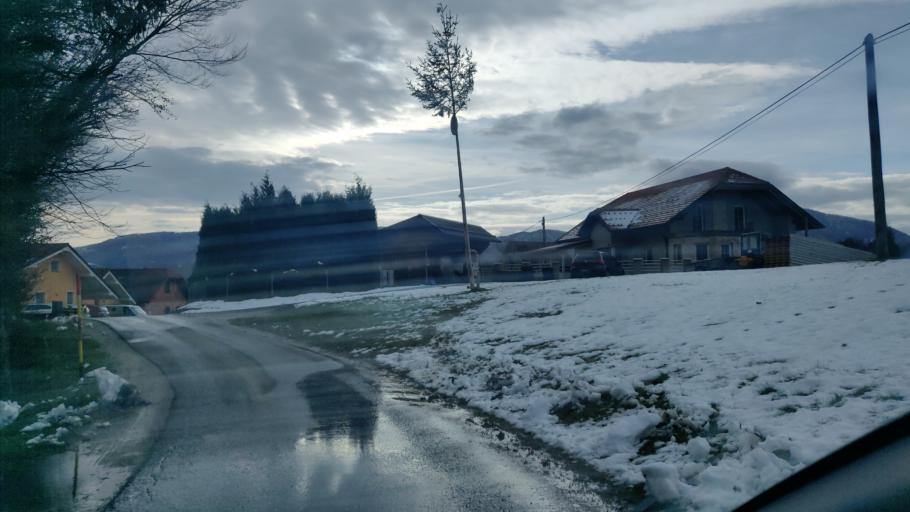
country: SI
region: Makole
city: Makole
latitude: 46.3291
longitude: 15.6558
